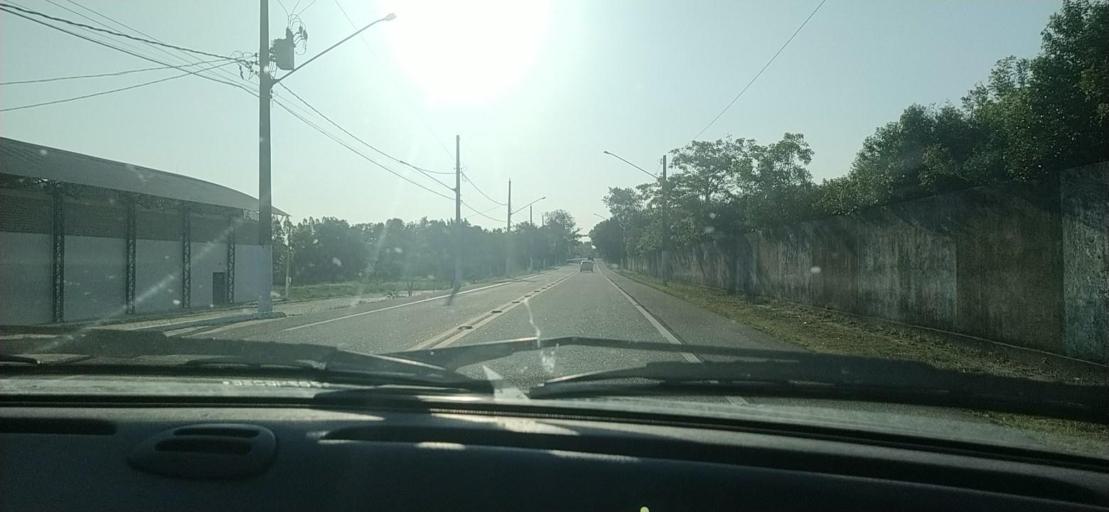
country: BR
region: Espirito Santo
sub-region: Conceicao Da Barra
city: Conceicao da Barra
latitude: -18.5673
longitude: -39.7564
